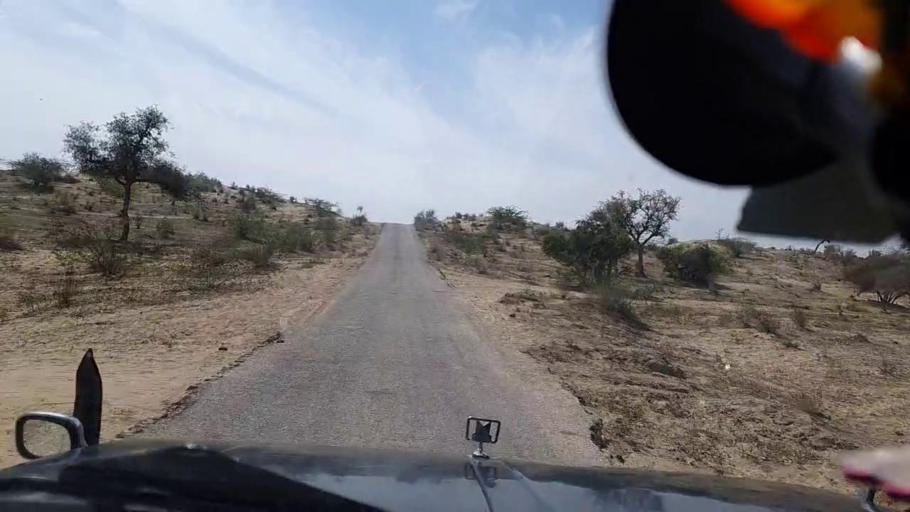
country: PK
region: Sindh
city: Diplo
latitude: 24.4192
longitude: 69.5838
